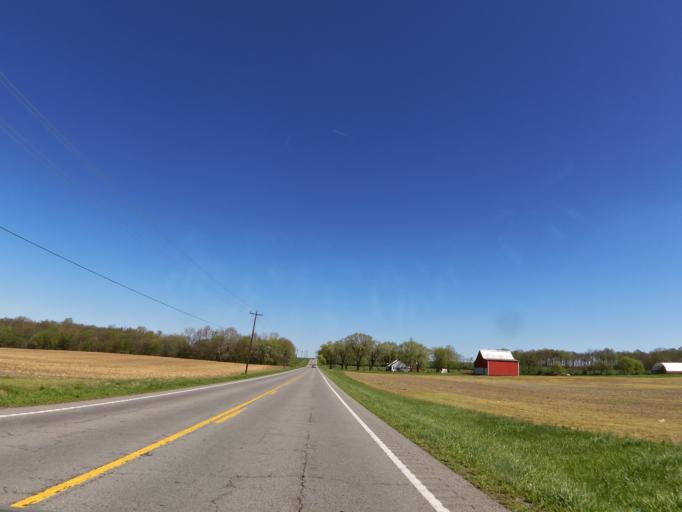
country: US
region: Tennessee
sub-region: Robertson County
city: Springfield
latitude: 36.5800
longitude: -86.8559
